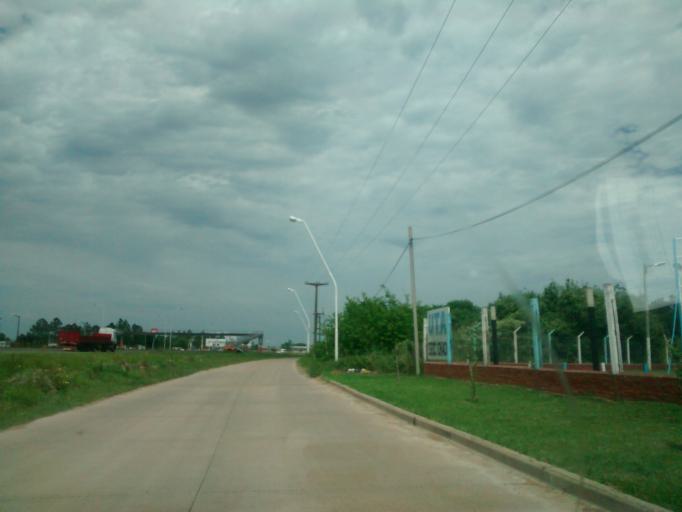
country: AR
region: Chaco
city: Fontana
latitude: -27.4089
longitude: -58.9856
